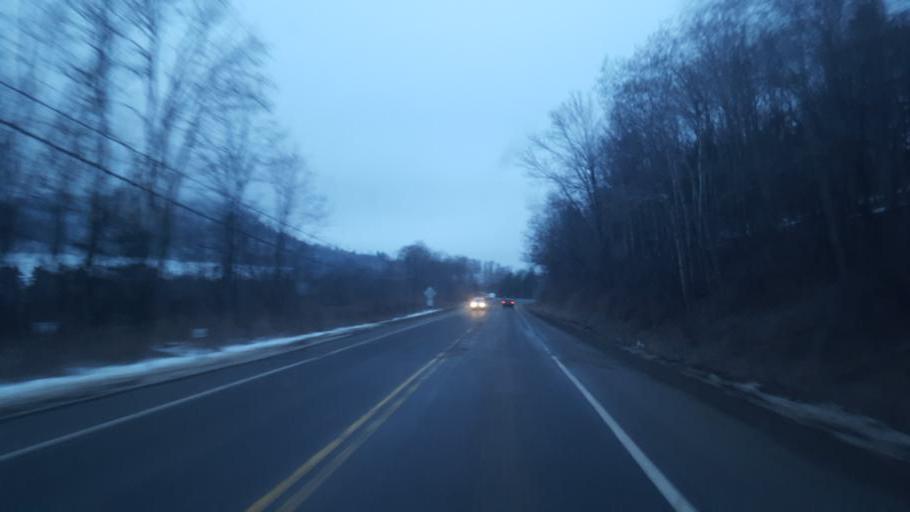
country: US
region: Pennsylvania
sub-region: Potter County
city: Coudersport
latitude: 41.7664
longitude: -78.1213
